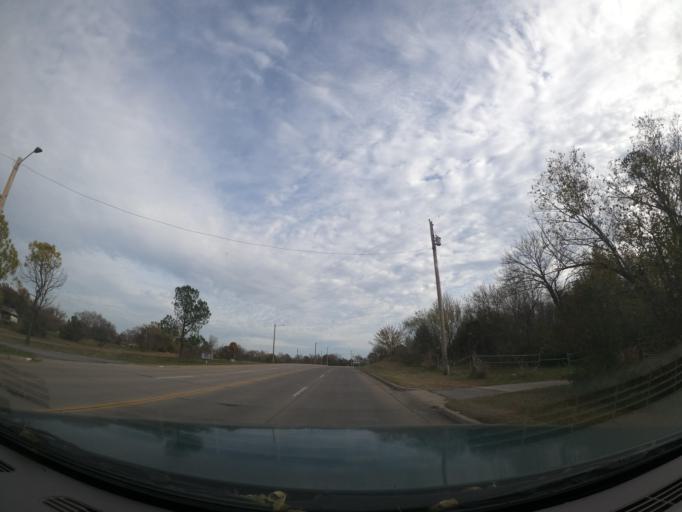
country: US
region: Oklahoma
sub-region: Tulsa County
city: Turley
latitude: 36.2111
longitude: -95.9951
